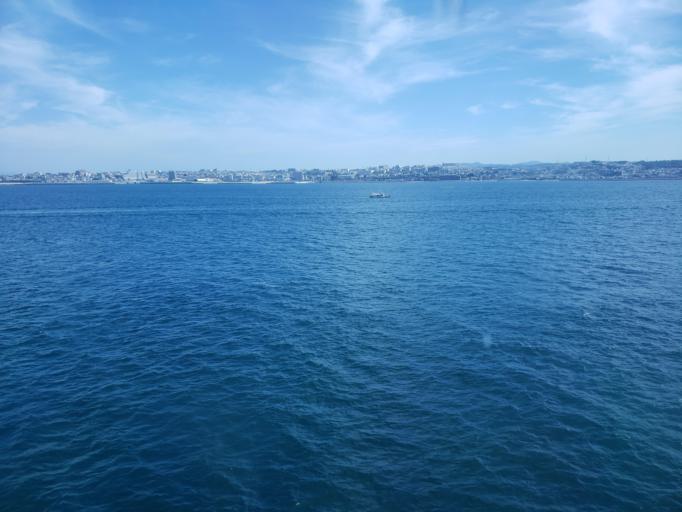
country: JP
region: Hyogo
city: Akashi
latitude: 34.6244
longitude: 135.0140
